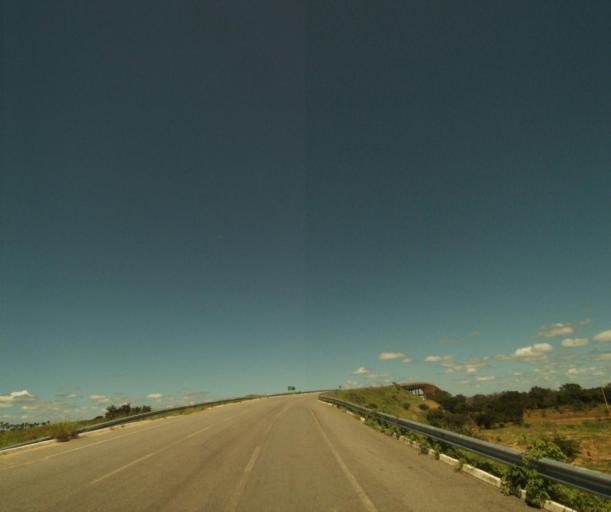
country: BR
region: Bahia
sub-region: Carinhanha
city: Carinhanha
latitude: -14.3276
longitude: -43.7639
